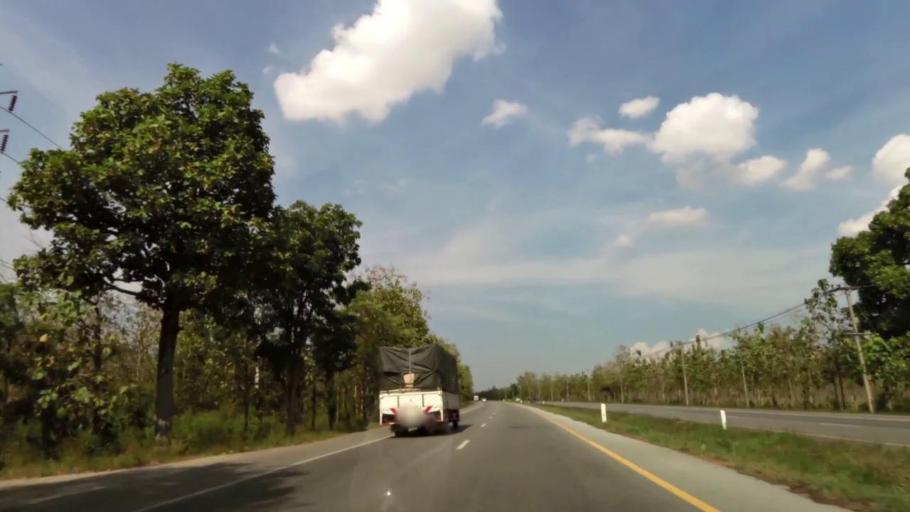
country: TH
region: Uttaradit
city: Thong Saen Khan
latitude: 17.5015
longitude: 100.2307
